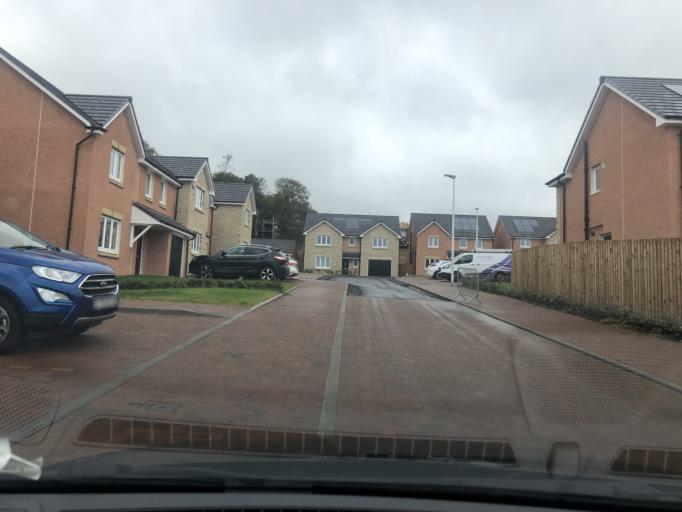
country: GB
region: Scotland
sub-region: Midlothian
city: Penicuik
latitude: 55.8432
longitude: -3.2211
